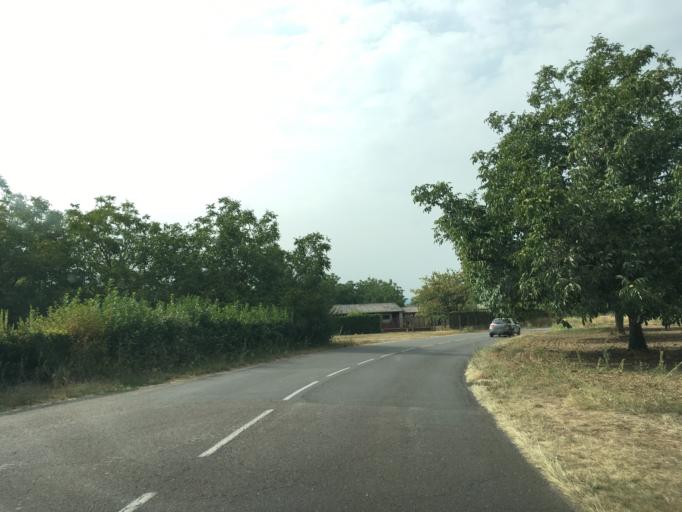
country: FR
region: Midi-Pyrenees
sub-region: Departement du Lot
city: Souillac
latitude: 44.8603
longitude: 1.5003
